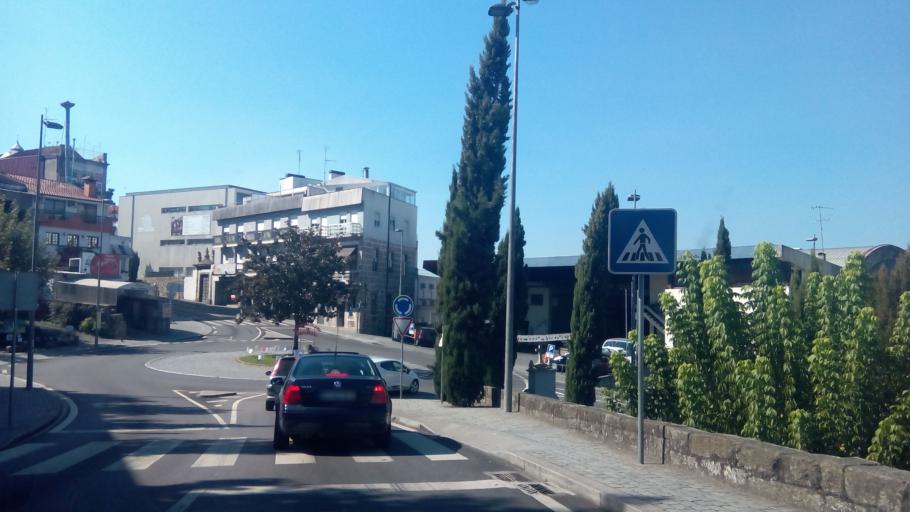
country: PT
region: Porto
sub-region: Penafiel
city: Penafiel
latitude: 41.2074
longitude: -8.2819
